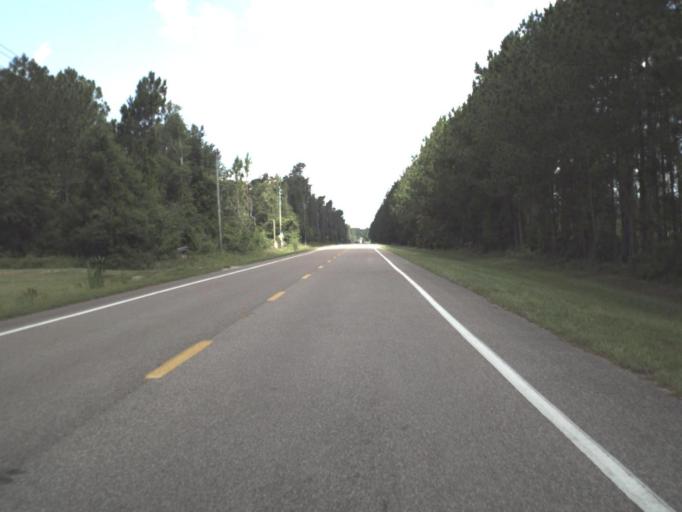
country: US
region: Florida
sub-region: Putnam County
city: East Palatka
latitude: 29.5799
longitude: -81.5575
